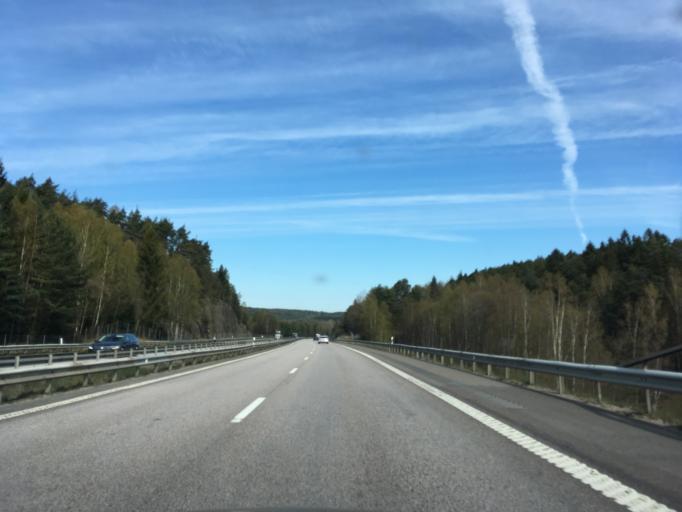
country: SE
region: Halland
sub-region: Kungsbacka Kommun
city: Fjaeras kyrkby
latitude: 57.4011
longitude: 12.1844
